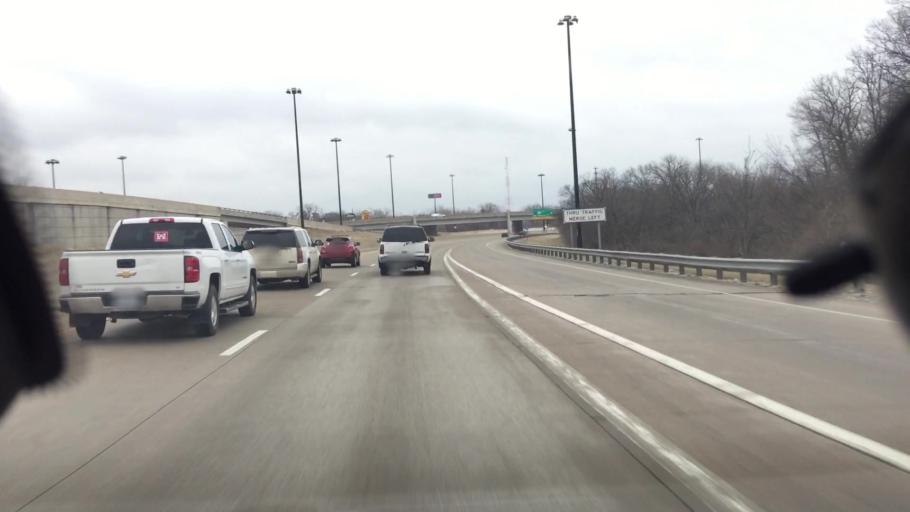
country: US
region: Illinois
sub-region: Peoria County
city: West Peoria
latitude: 40.7367
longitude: -89.6273
